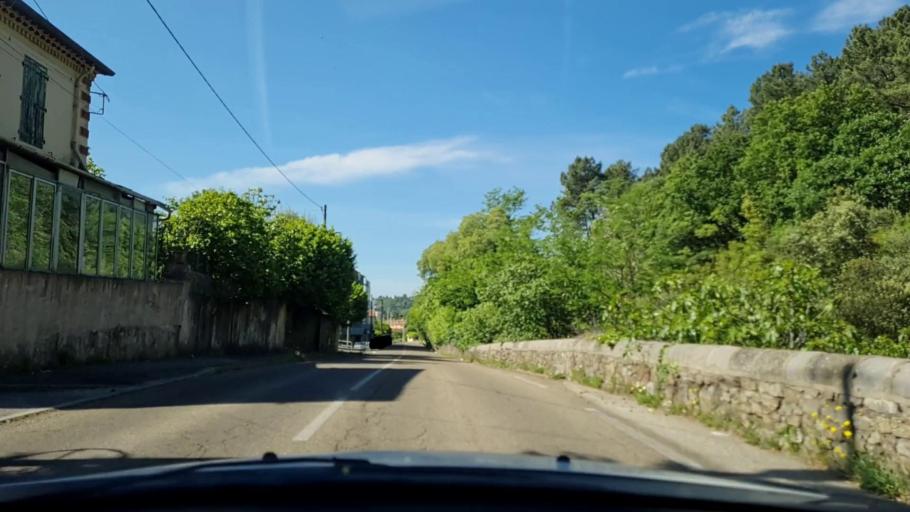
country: FR
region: Languedoc-Roussillon
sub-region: Departement du Gard
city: Ales
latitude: 44.1402
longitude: 4.0743
